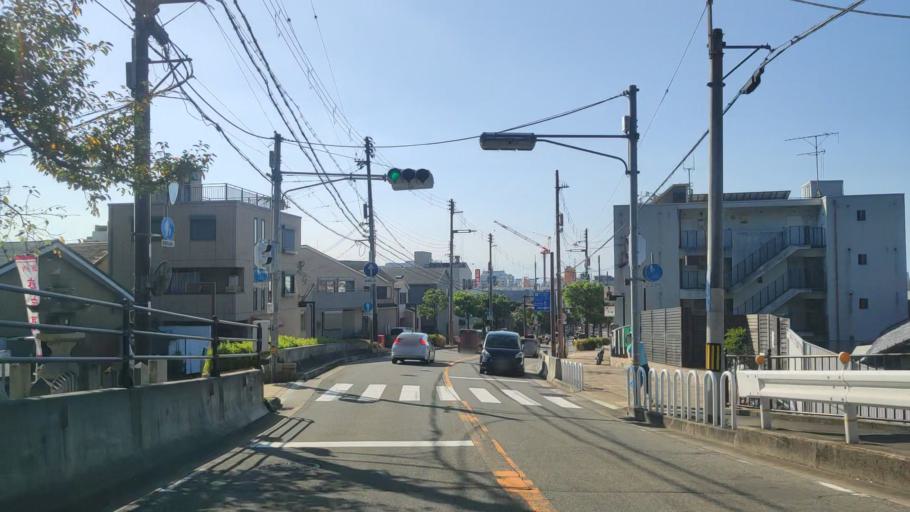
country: JP
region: Hyogo
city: Kobe
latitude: 34.6928
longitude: 135.1669
